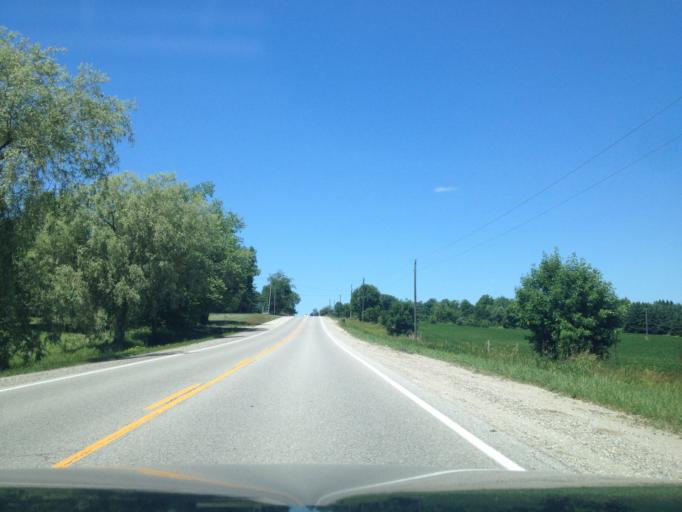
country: CA
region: Ontario
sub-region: Wellington County
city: Guelph
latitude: 43.6298
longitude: -80.2340
